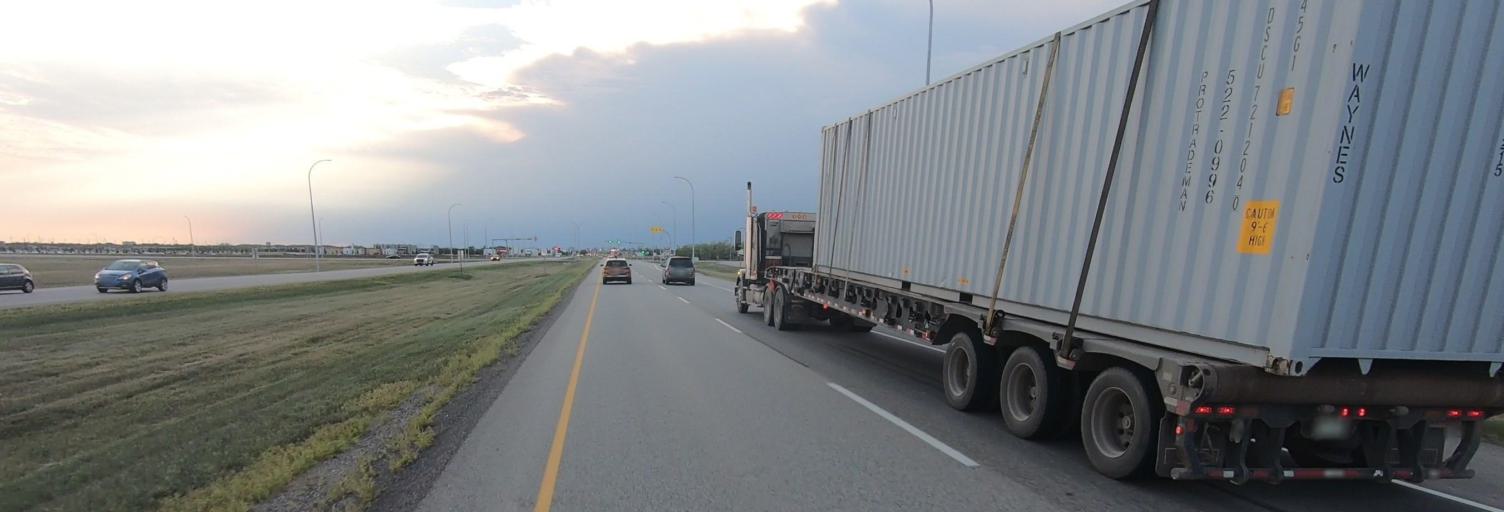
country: CA
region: Saskatchewan
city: Pilot Butte
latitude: 50.4477
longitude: -104.4988
